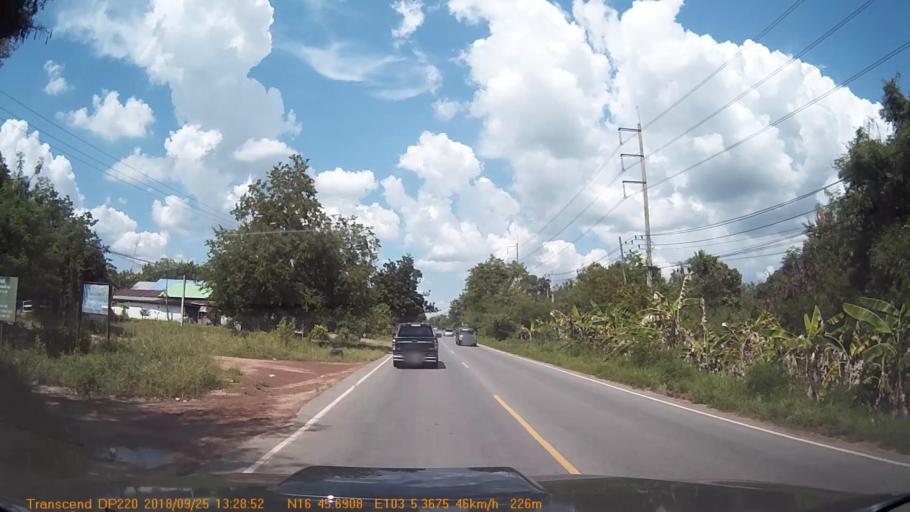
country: TH
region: Khon Kaen
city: Kranuan
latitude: 16.7615
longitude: 103.0895
